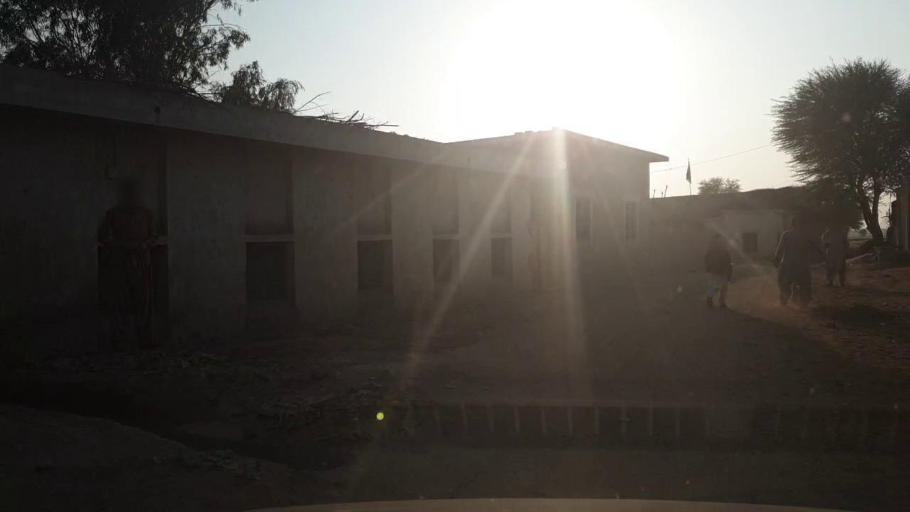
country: PK
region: Sindh
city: Hala
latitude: 25.8594
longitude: 68.4043
